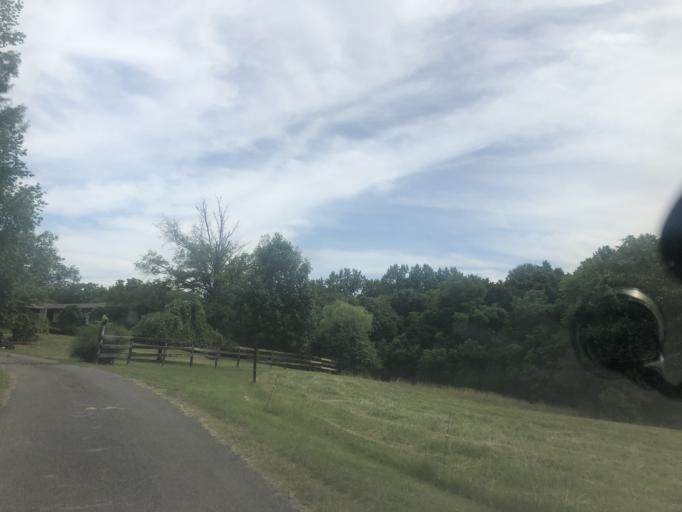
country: US
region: Tennessee
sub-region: Davidson County
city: Lakewood
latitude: 36.2150
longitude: -86.6621
